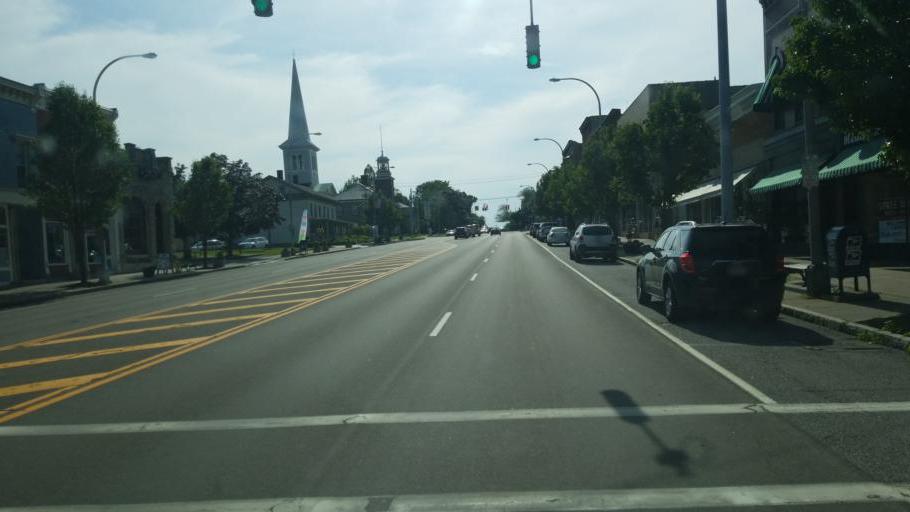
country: US
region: New York
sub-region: Genesee County
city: Le Roy
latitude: 42.9777
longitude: -77.9905
